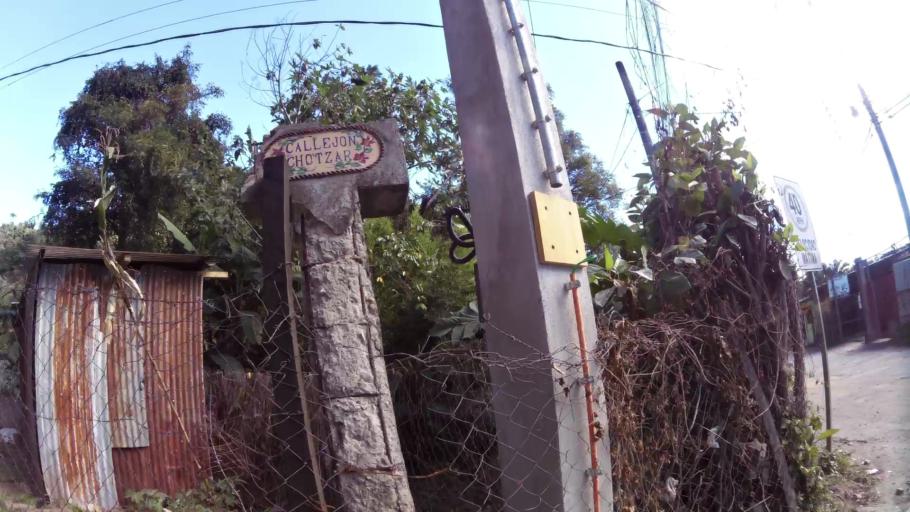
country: GT
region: Solola
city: Panajachel
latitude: 14.7396
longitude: -91.1511
